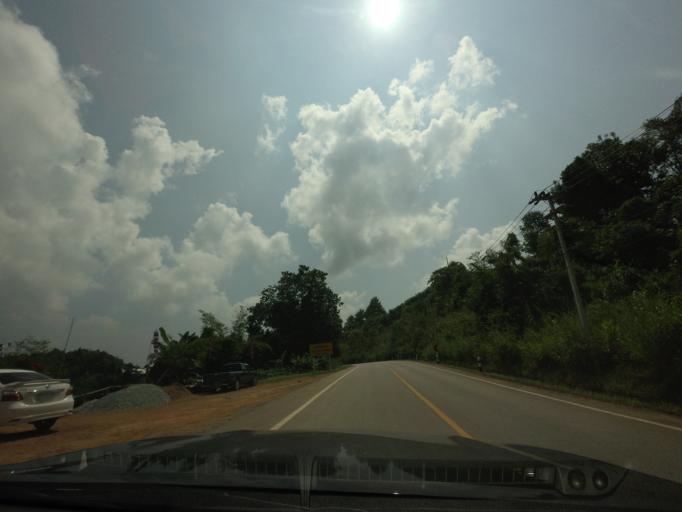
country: TH
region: Nan
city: Santi Suk
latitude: 18.9149
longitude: 100.8816
